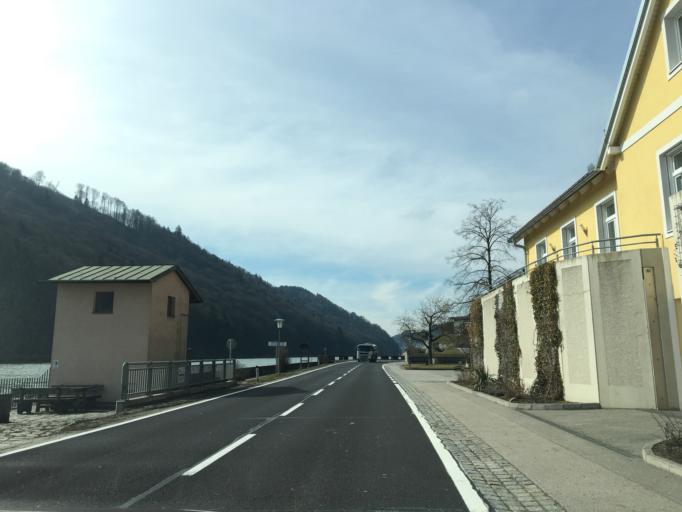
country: AT
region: Lower Austria
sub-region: Politischer Bezirk Melk
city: Nochling
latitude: 48.2320
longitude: 14.9371
